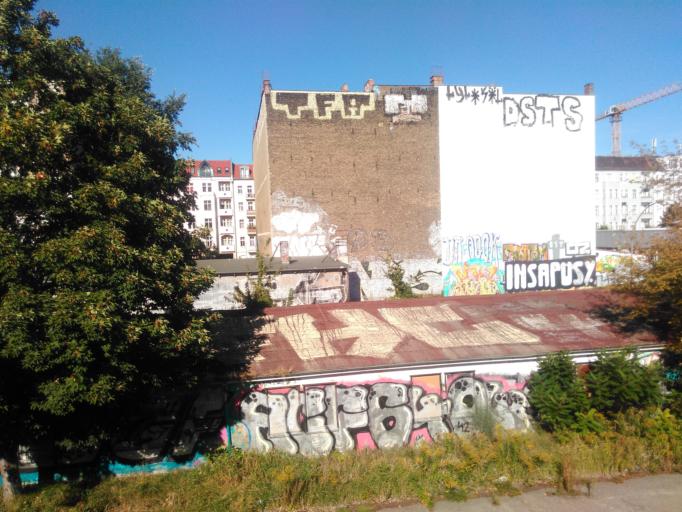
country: DE
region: Berlin
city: Treptow Bezirk
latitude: 52.4979
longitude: 13.4670
